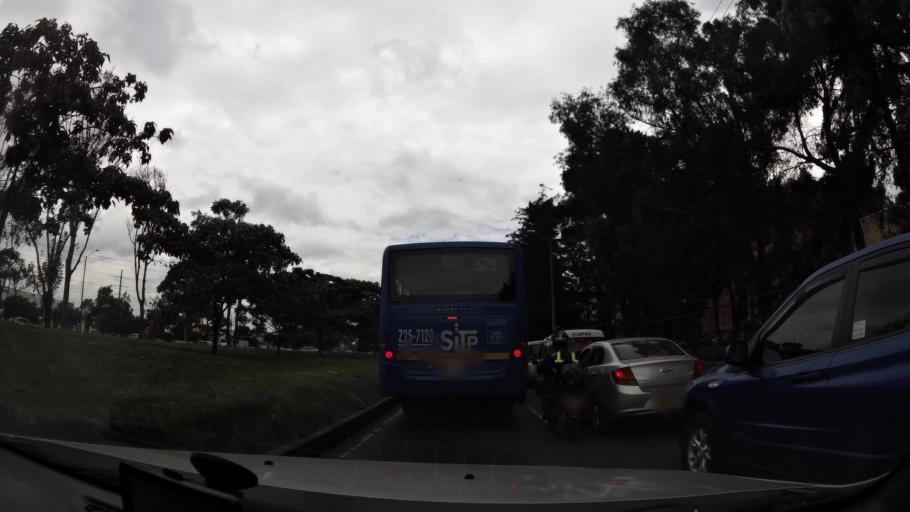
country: CO
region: Bogota D.C.
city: Bogota
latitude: 4.6259
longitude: -74.0898
